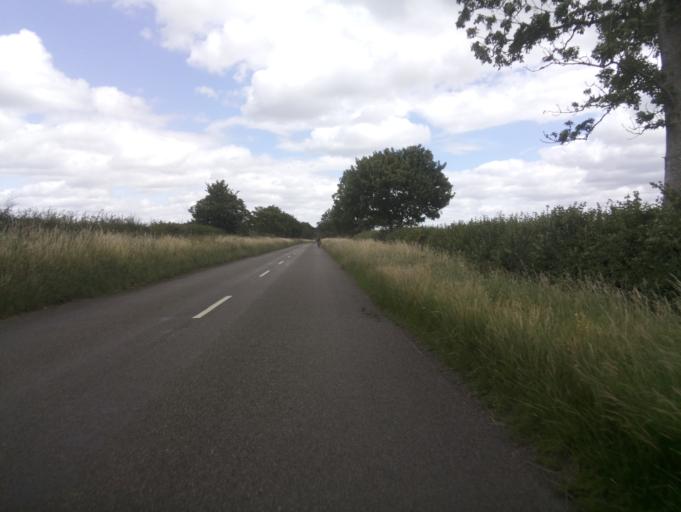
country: GB
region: England
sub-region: Nottinghamshire
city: Cotgrave
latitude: 52.8517
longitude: -1.0522
